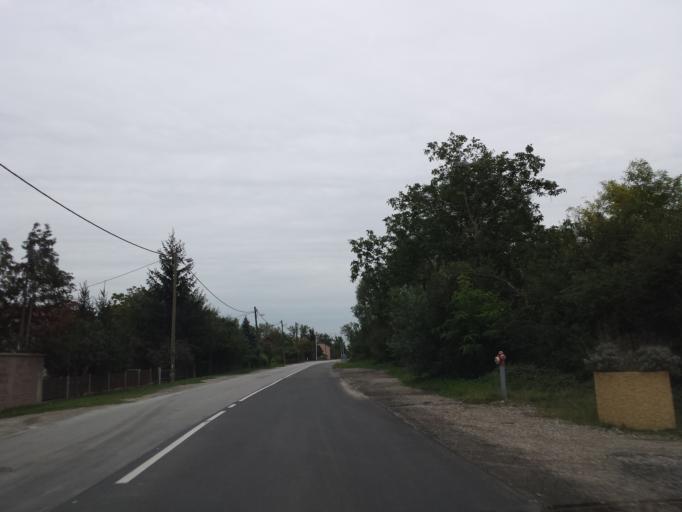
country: HR
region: Grad Zagreb
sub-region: Sesvete
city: Sesvete
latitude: 45.7914
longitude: 16.1311
